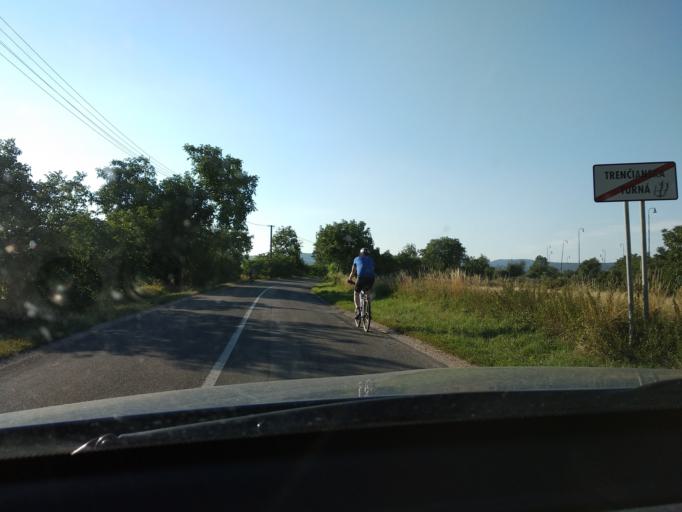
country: SK
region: Trenciansky
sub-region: Okres Trencin
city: Trencin
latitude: 48.8594
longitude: 18.0184
